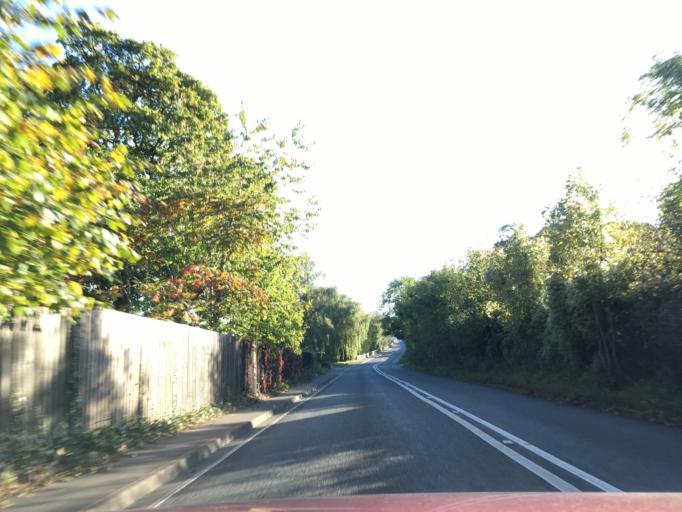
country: GB
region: England
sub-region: Bristol
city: Bristol
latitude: 51.4481
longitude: -2.6263
